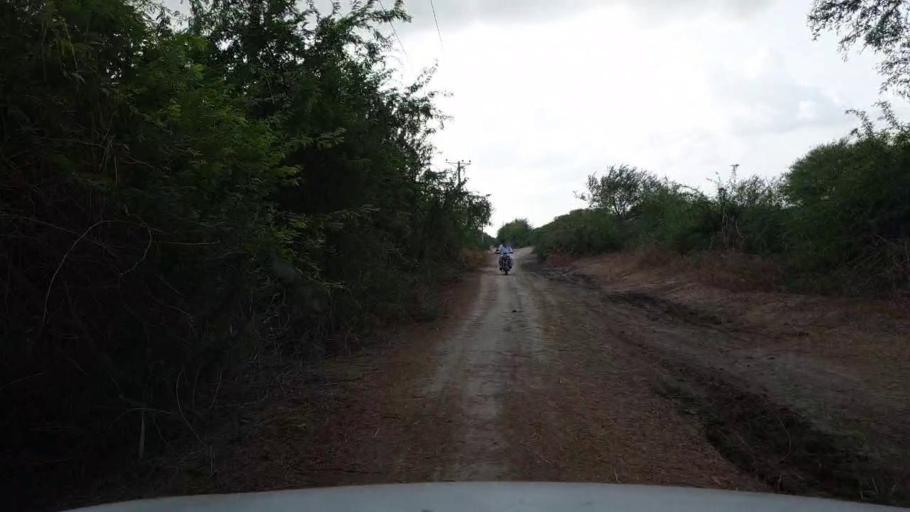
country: PK
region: Sindh
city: Kario
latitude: 24.7552
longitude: 68.6103
